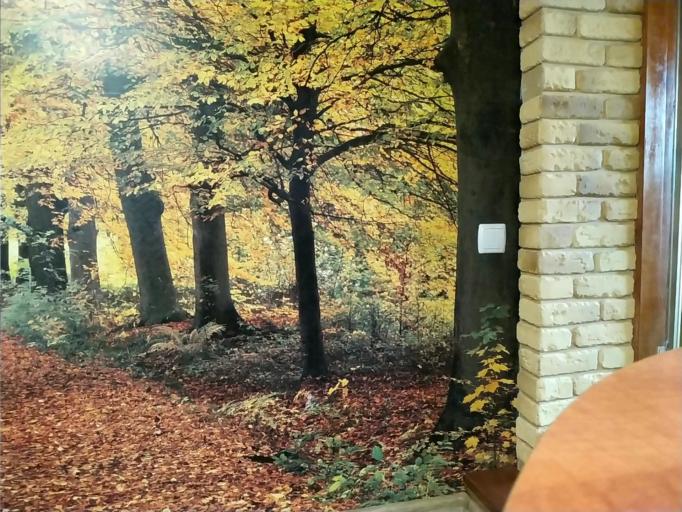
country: RU
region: Leningrad
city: Tolmachevo
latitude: 58.9302
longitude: 29.7189
